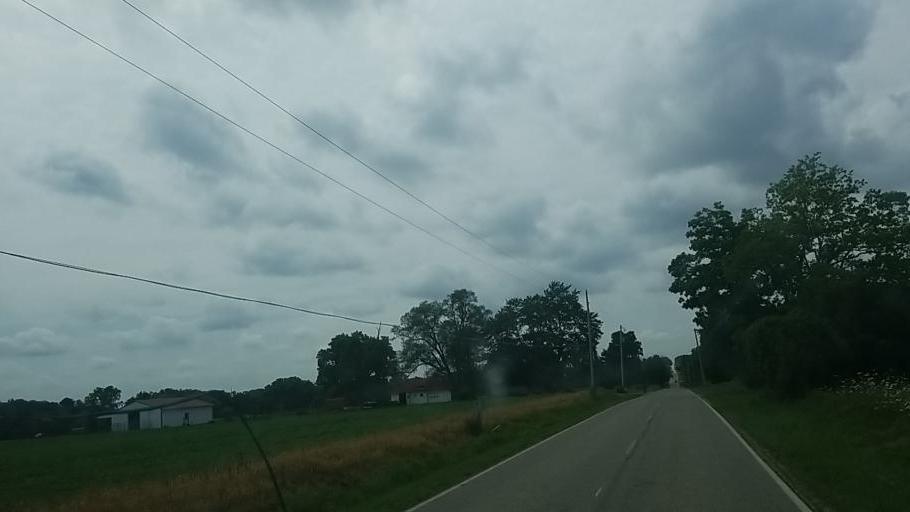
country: US
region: Ohio
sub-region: Fairfield County
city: Lithopolis
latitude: 39.7518
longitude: -82.8397
